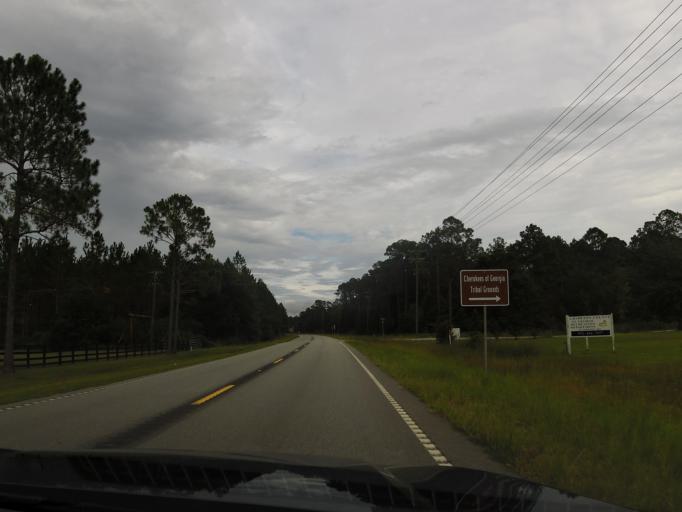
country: US
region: Florida
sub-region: Nassau County
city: Hilliard
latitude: 30.5212
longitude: -82.0524
